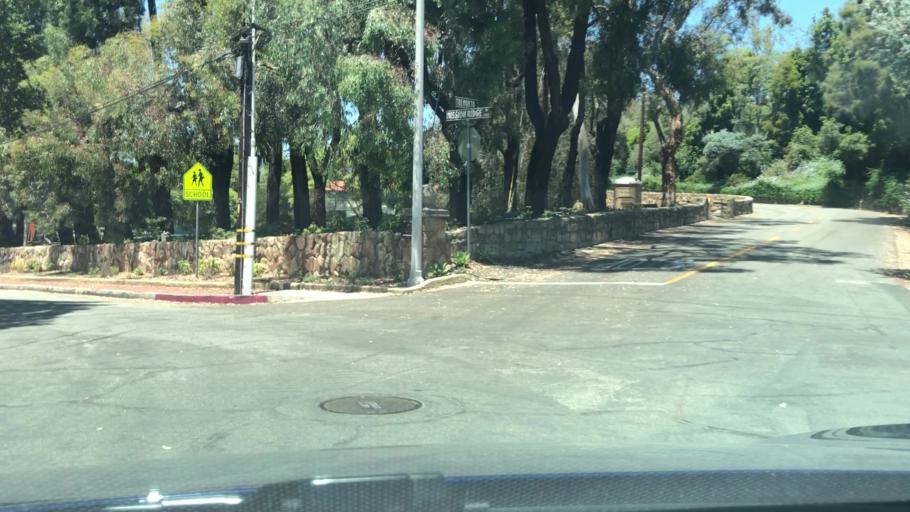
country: US
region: California
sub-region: Santa Barbara County
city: Mission Canyon
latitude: 34.4406
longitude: -119.7074
